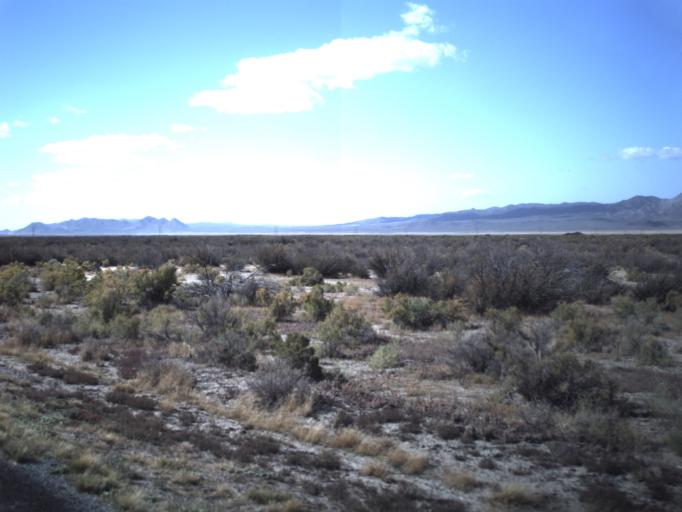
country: US
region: Utah
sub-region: Beaver County
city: Milford
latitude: 38.5912
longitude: -112.9882
